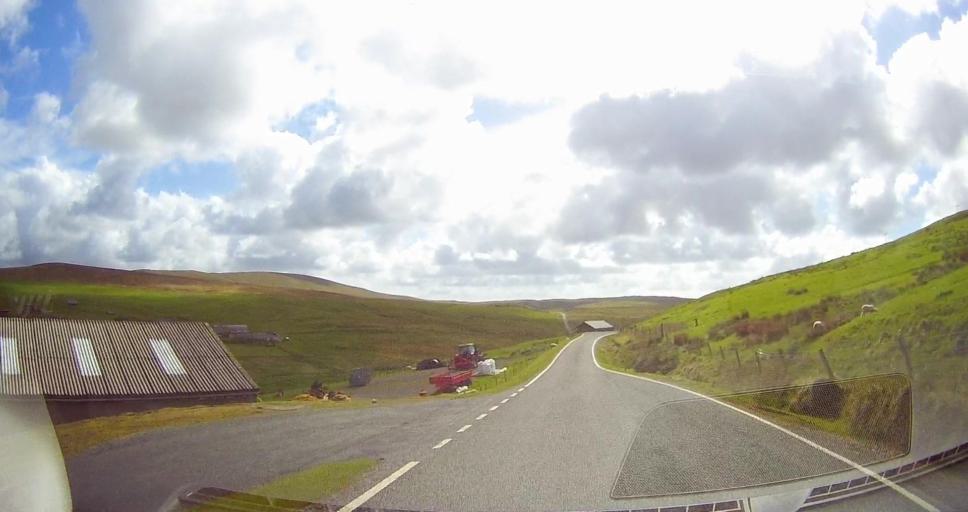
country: GB
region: Scotland
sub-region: Shetland Islands
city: Lerwick
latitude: 60.5279
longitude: -1.3678
